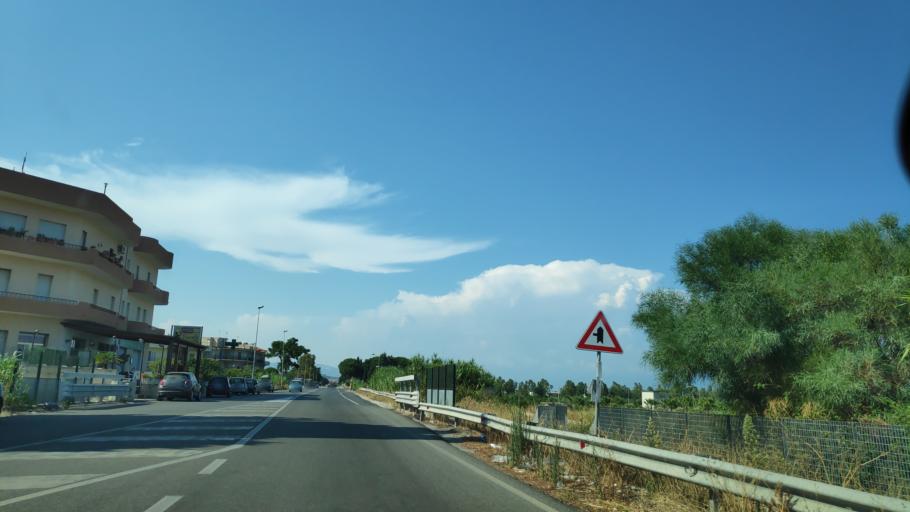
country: IT
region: Calabria
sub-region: Provincia di Catanzaro
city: Isca Marina
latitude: 38.6037
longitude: 16.5573
